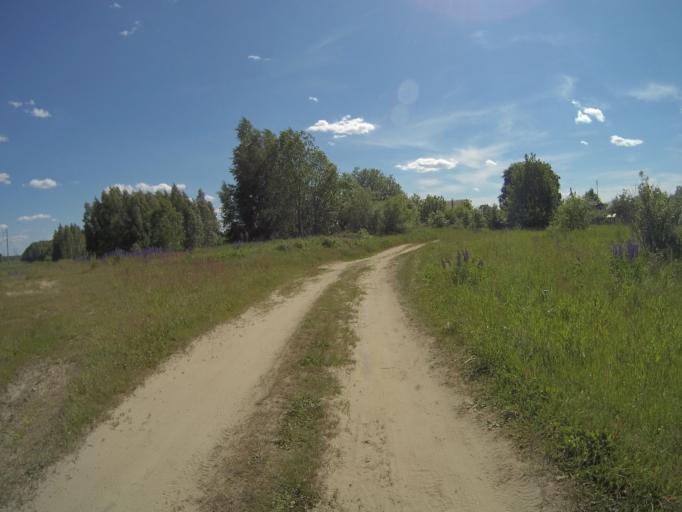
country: RU
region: Vladimir
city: Golovino
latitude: 55.9864
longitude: 40.4024
